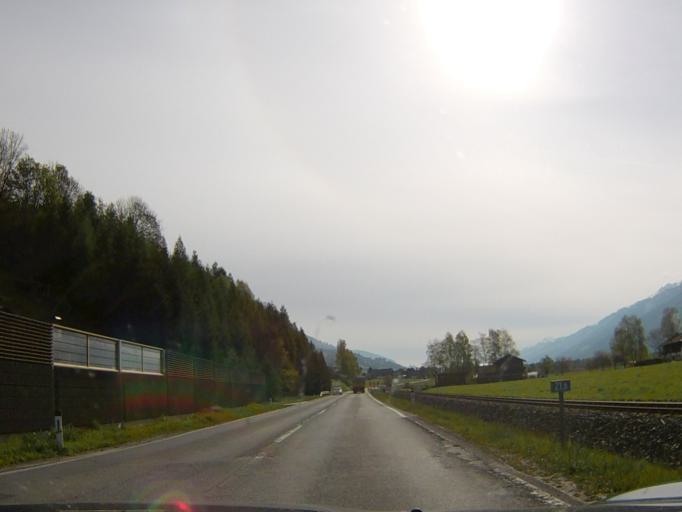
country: AT
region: Salzburg
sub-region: Politischer Bezirk Zell am See
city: Stuhlfelden
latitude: 47.2859
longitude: 12.5090
